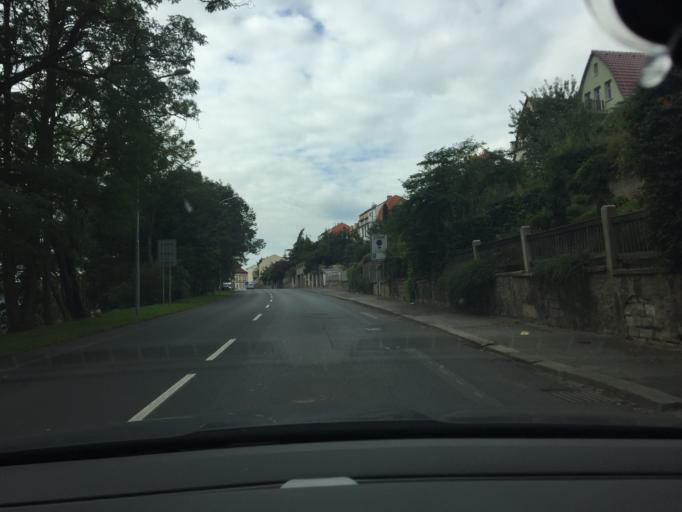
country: CZ
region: Ustecky
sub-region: Okres Litomerice
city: Litomerice
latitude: 50.5339
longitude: 14.1468
